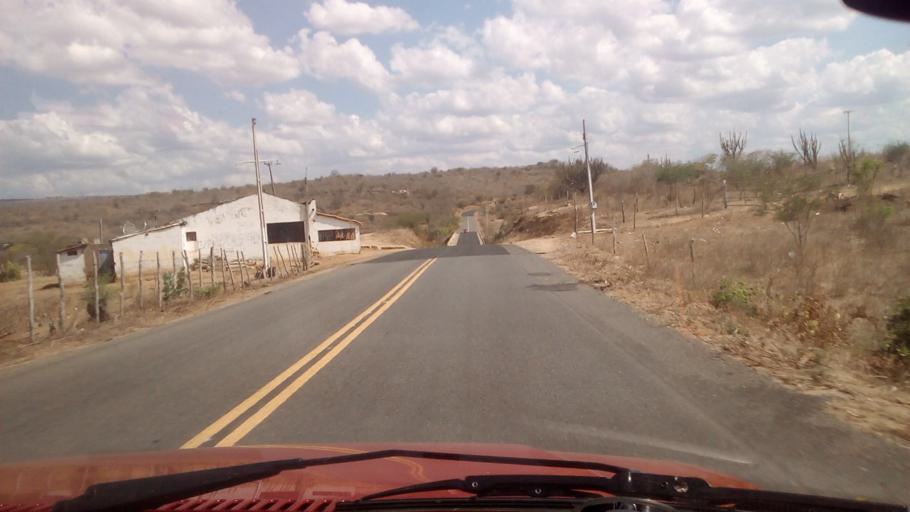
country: BR
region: Paraiba
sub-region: Cacimba De Dentro
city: Cacimba de Dentro
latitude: -6.6759
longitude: -35.7453
